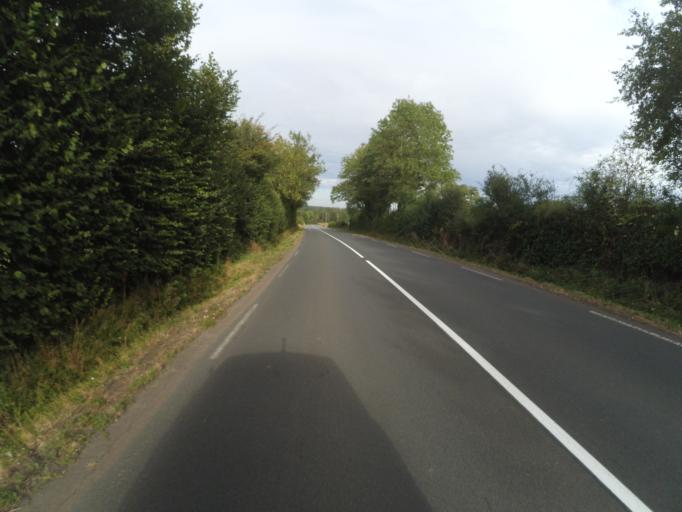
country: FR
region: Poitou-Charentes
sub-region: Departement des Deux-Sevres
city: Saint-Amand-sur-Sevre
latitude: 46.9285
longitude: -0.7797
